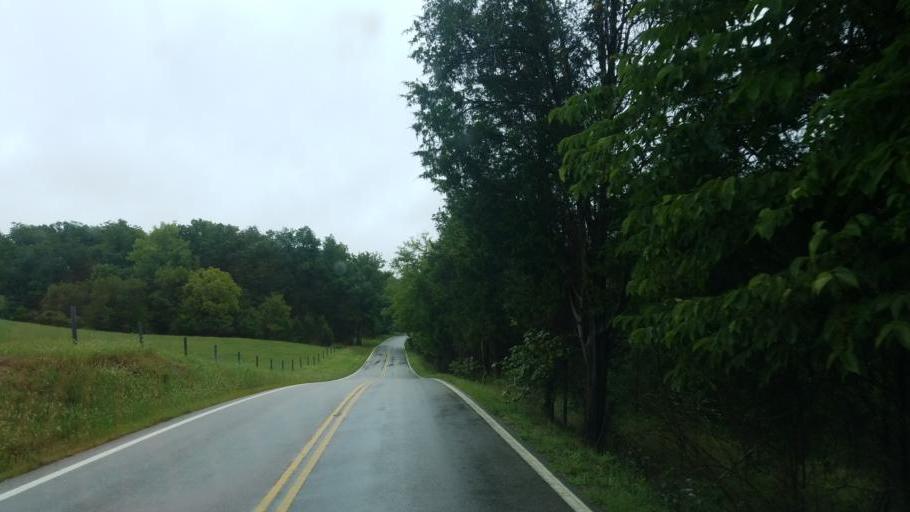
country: US
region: Ohio
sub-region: Adams County
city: West Union
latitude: 38.7824
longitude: -83.5379
